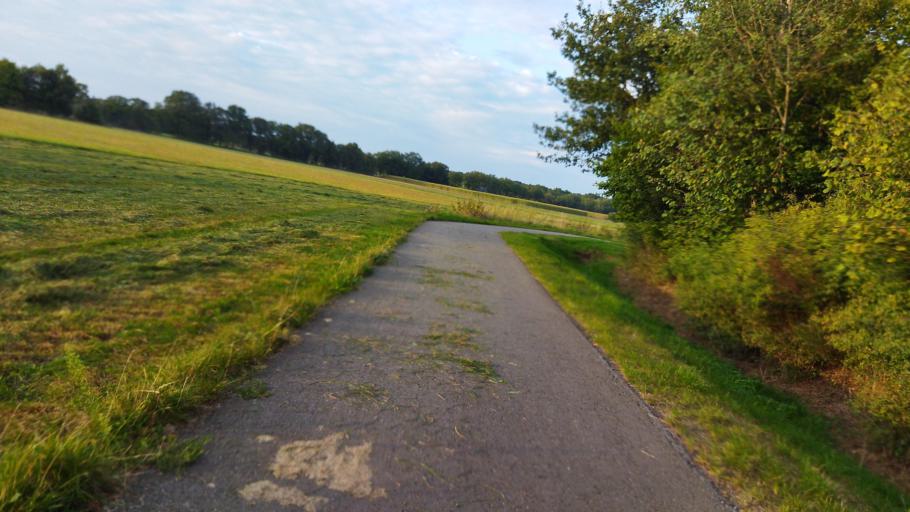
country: DE
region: Lower Saxony
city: Glandorf
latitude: 52.0861
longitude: 8.0419
